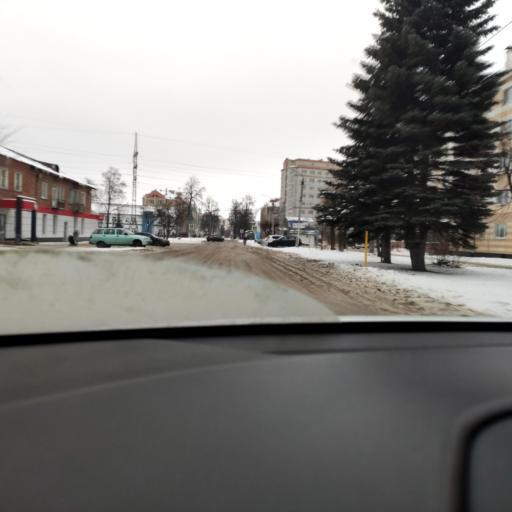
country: RU
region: Tatarstan
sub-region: Zelenodol'skiy Rayon
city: Zelenodolsk
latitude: 55.8519
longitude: 48.4853
